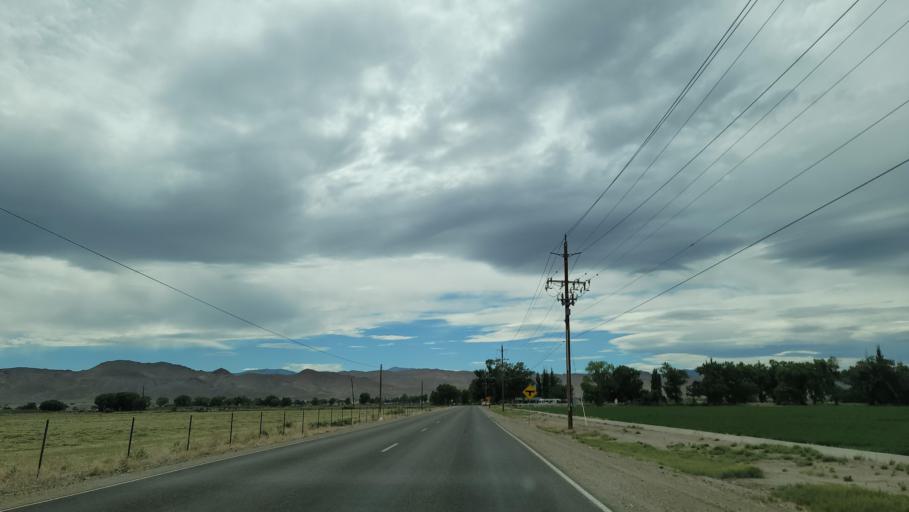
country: US
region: Nevada
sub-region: Lyon County
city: Yerington
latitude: 39.0481
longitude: -119.1774
